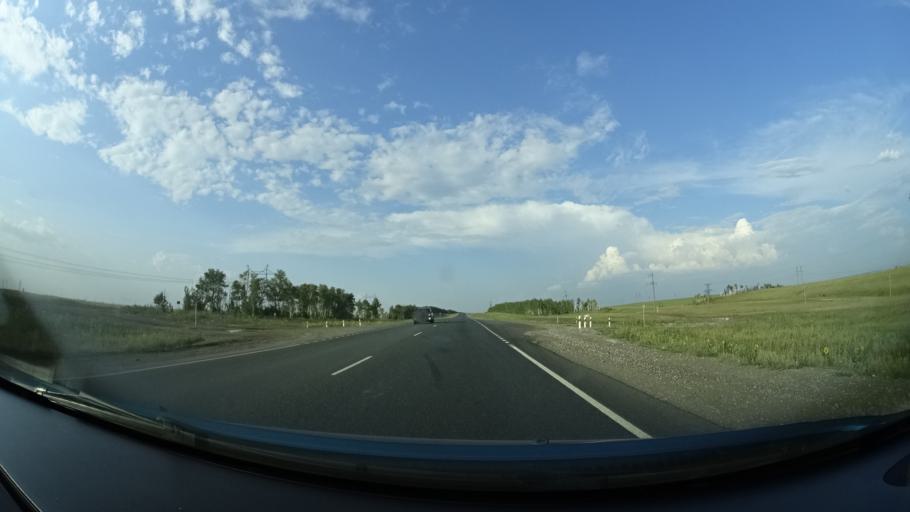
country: RU
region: Samara
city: Sukhodol
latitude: 53.7096
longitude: 50.8148
